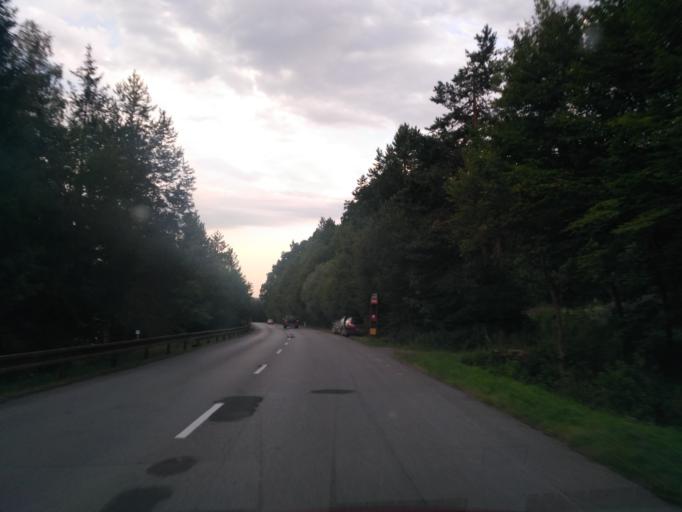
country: SK
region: Presovsky
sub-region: Okres Presov
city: Presov
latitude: 48.9771
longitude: 21.1718
